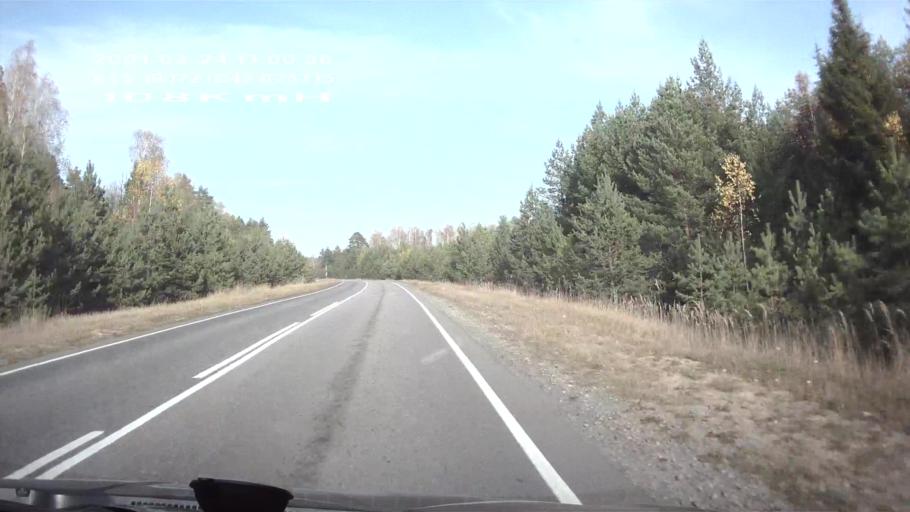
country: RU
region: Chuvashia
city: Buinsk
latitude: 55.1907
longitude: 47.0737
